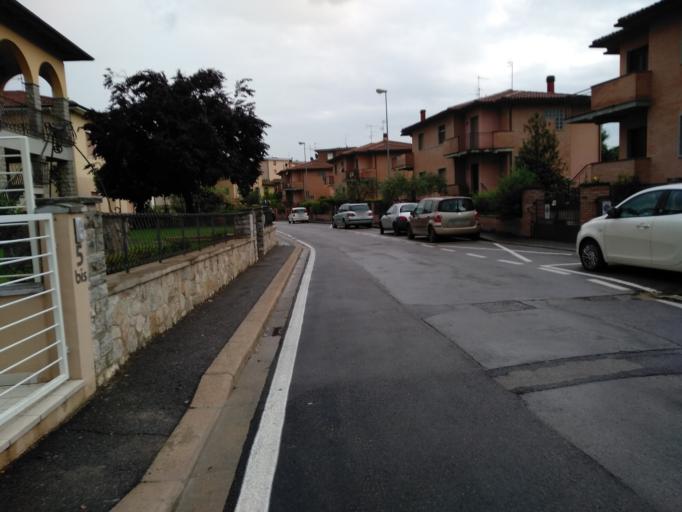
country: IT
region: Tuscany
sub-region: Province of Arezzo
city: San Giovanni Valdarno
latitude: 43.5614
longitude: 11.5271
